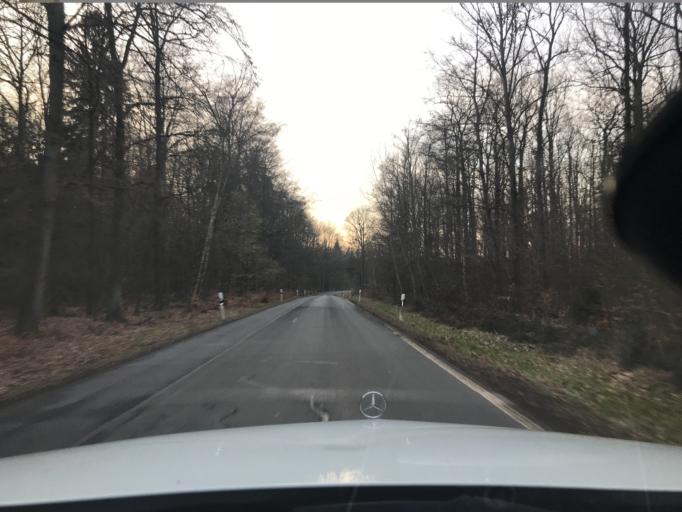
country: DE
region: Thuringia
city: Emleben
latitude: 50.9058
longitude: 10.6564
